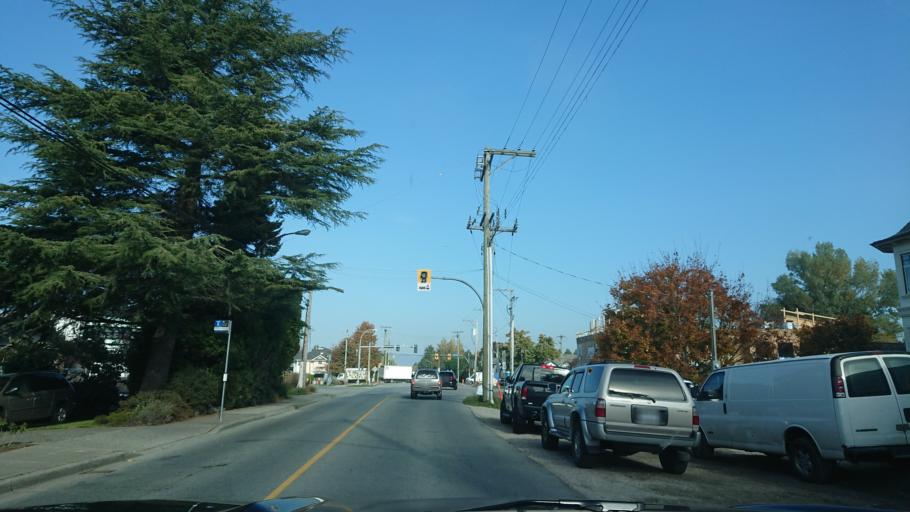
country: CA
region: British Columbia
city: Richmond
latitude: 49.1324
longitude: -123.1589
